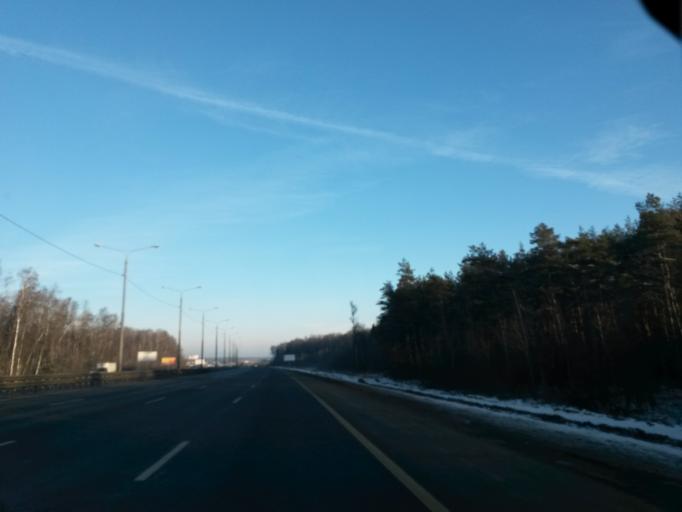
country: RU
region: Moskovskaya
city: Klimovsk
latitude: 55.3674
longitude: 37.6032
